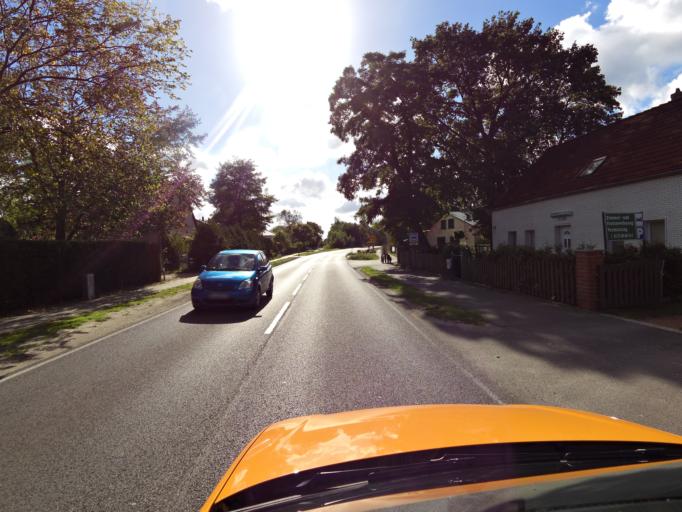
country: DE
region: Brandenburg
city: Michendorf
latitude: 52.3244
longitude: 13.1188
